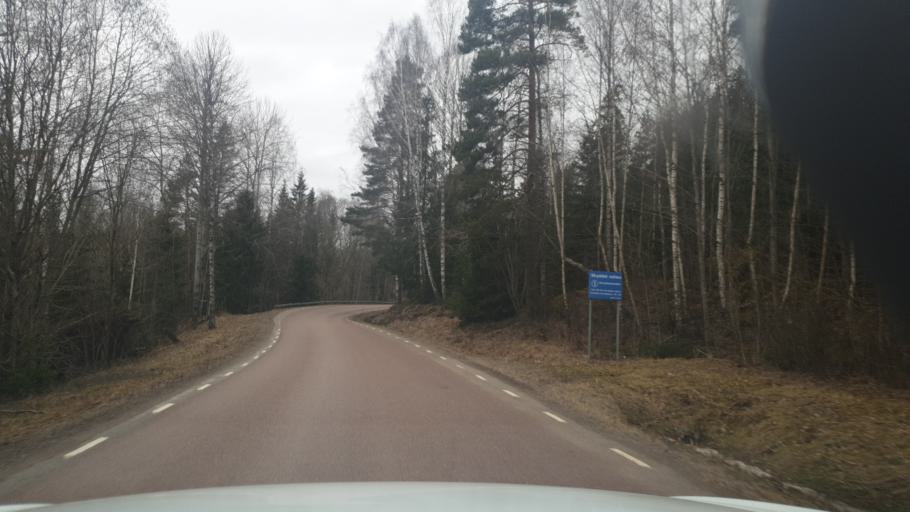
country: NO
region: Hedmark
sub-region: Eidskog
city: Skotterud
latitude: 59.8140
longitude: 12.0235
